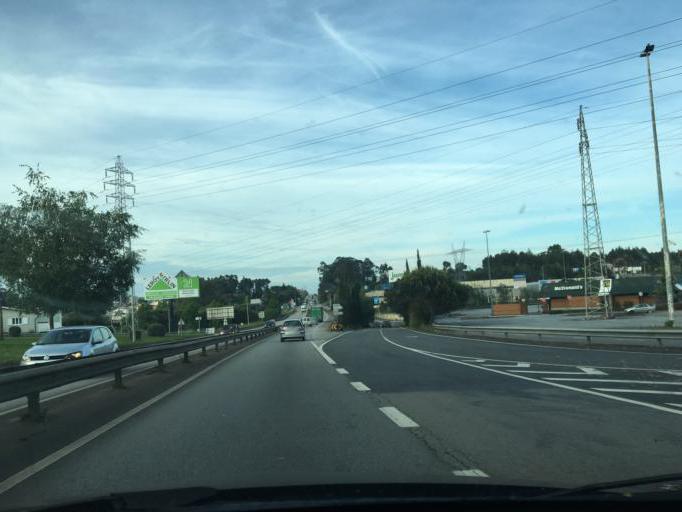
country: PT
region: Porto
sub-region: Maia
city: Maia
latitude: 41.2498
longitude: -8.6181
